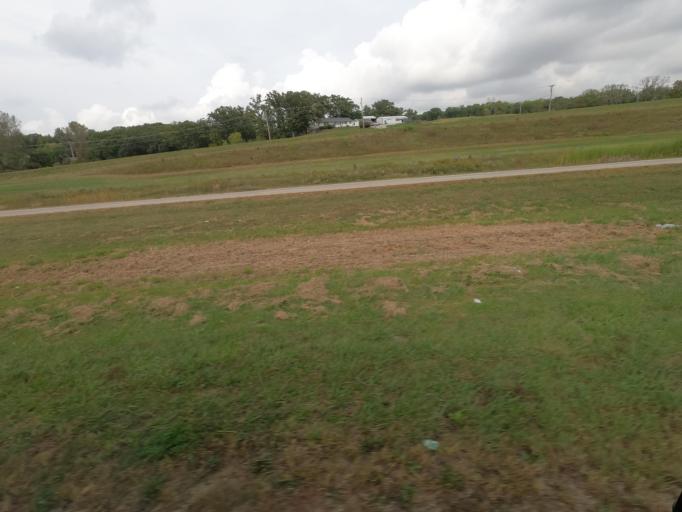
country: US
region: Iowa
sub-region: Wapello County
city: Ottumwa
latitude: 40.9996
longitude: -92.3454
